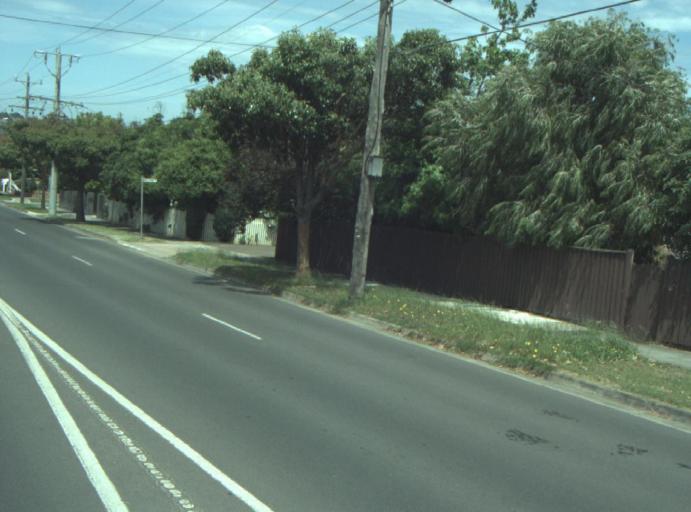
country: AU
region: Victoria
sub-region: Greater Geelong
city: Geelong West
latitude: -38.1555
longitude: 144.3336
